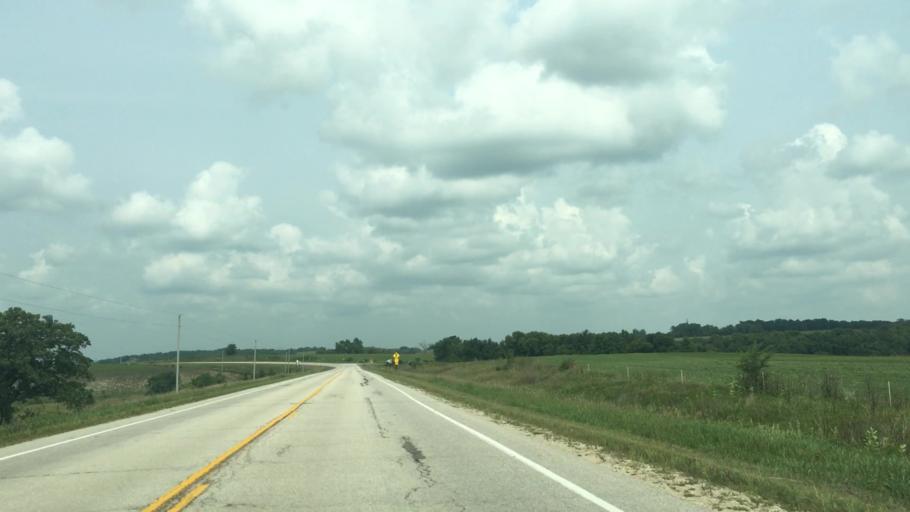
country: US
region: Minnesota
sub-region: Fillmore County
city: Preston
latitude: 43.6849
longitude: -91.9426
